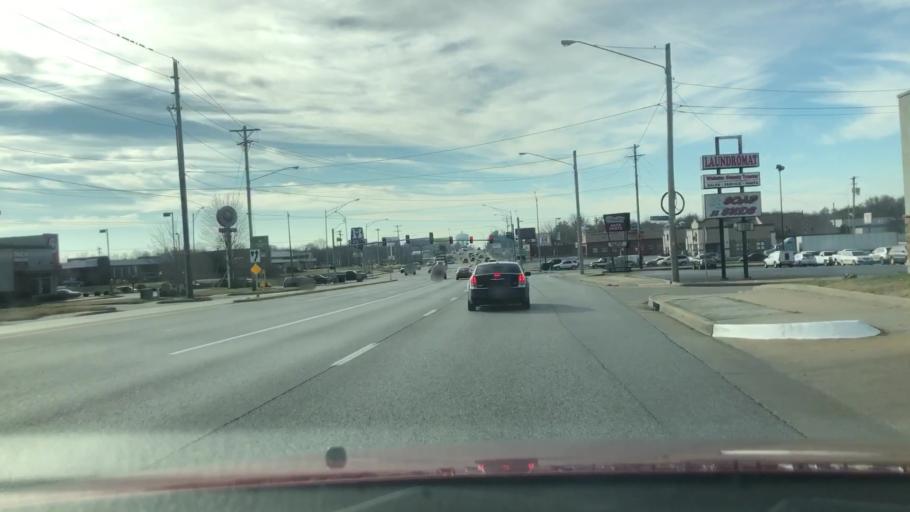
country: US
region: Missouri
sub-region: Greene County
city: Springfield
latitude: 37.2159
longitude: -93.2618
